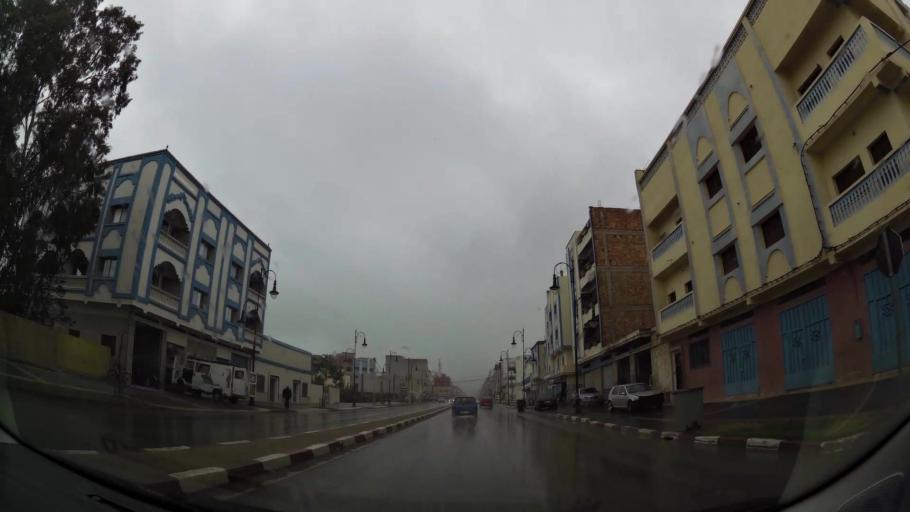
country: MA
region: Taza-Al Hoceima-Taounate
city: Imzourene
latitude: 35.1103
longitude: -3.8415
